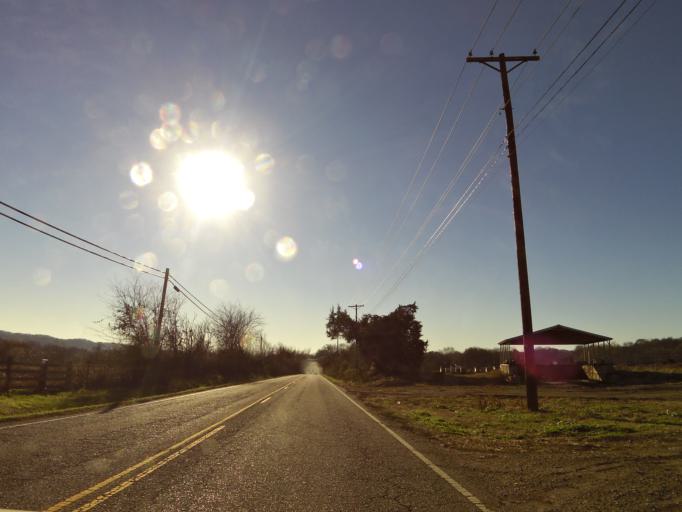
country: US
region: Tennessee
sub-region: Anderson County
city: Clinton
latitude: 36.0132
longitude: -84.0655
